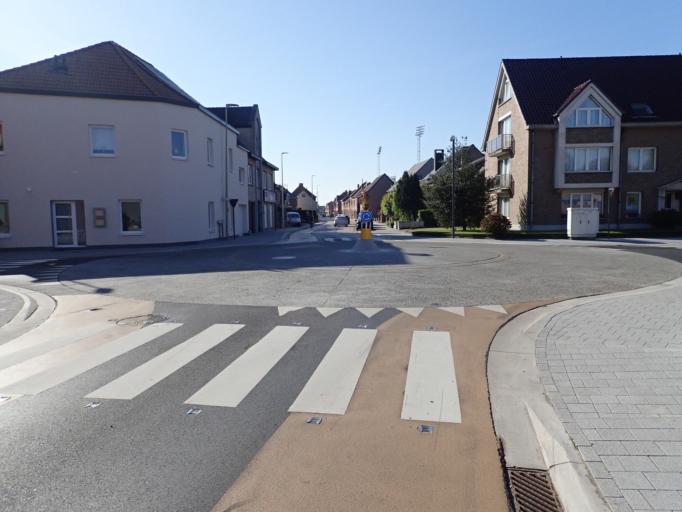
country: BE
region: Flanders
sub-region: Provincie Oost-Vlaanderen
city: Beveren
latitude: 51.2161
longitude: 4.2456
